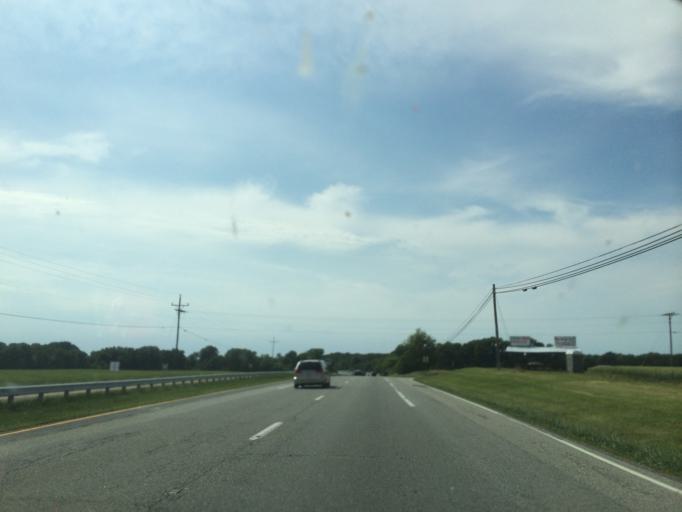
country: US
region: Maryland
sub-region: Queen Anne's County
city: Grasonville
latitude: 38.9719
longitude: -76.1228
